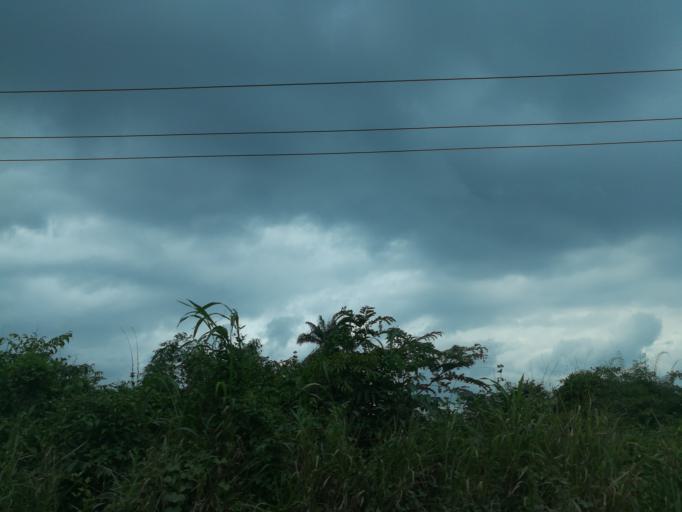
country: NG
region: Lagos
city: Ejirin
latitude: 6.6446
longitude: 3.8494
